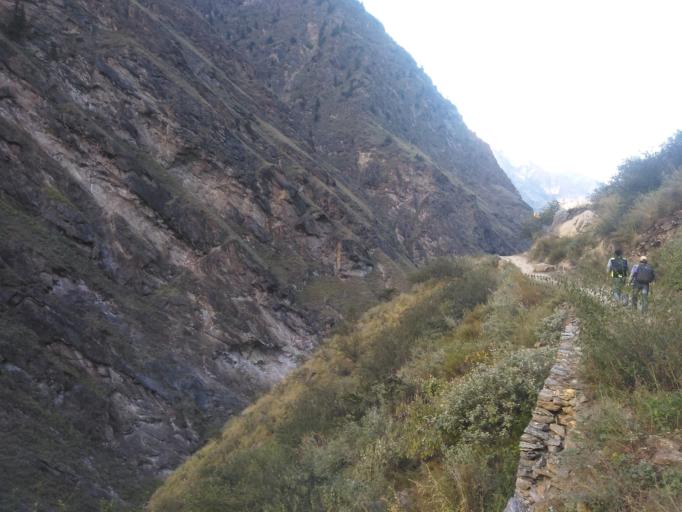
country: NP
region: Western Region
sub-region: Dhawalagiri Zone
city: Jomsom
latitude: 28.8779
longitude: 83.0095
